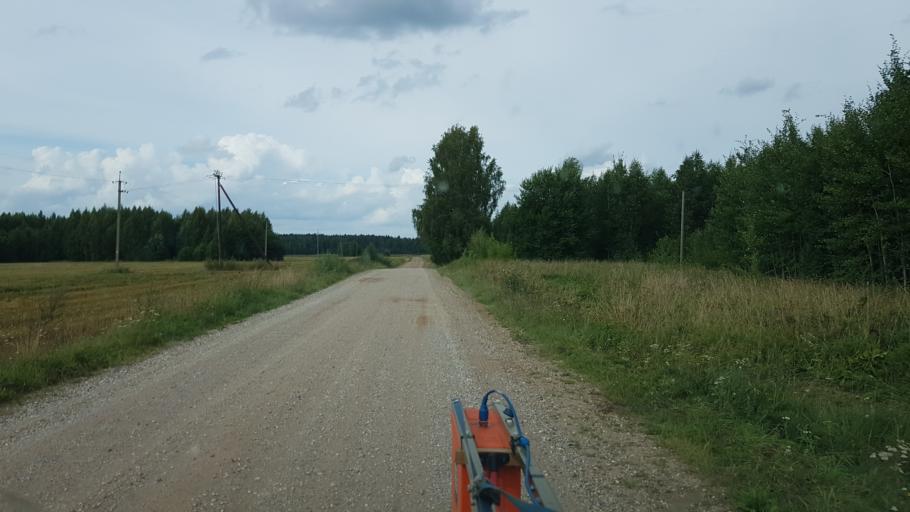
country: RU
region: Pskov
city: Pechory
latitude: 57.8067
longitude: 27.5087
